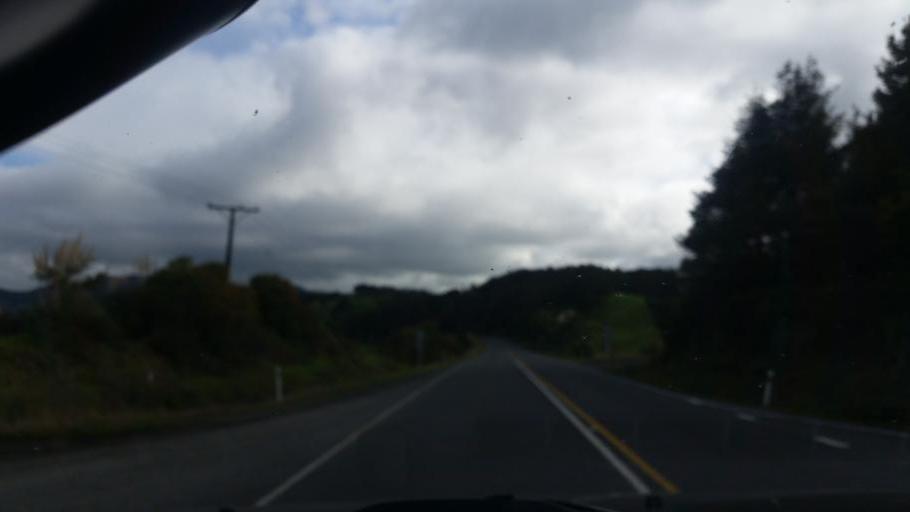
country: NZ
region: Northland
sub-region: Whangarei
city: Maungatapere
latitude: -35.8202
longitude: 174.0396
